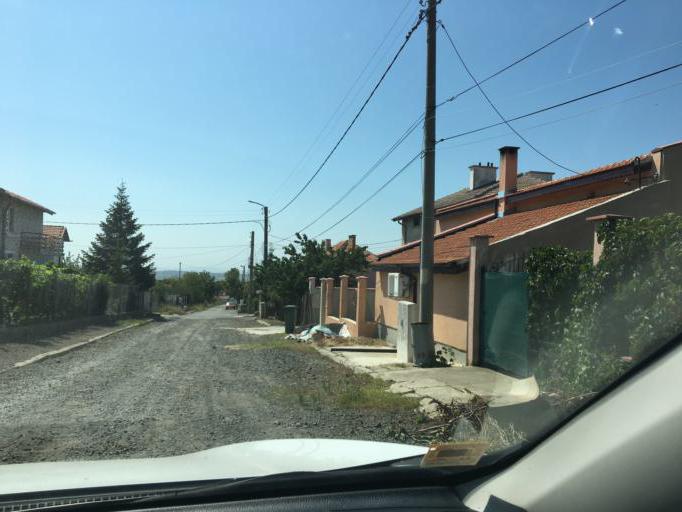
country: BG
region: Burgas
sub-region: Obshtina Kameno
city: Kameno
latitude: 42.6322
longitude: 27.3914
